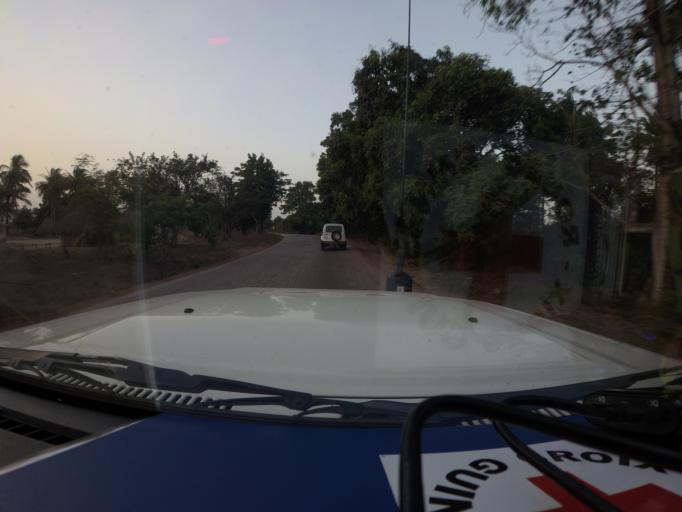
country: GN
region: Kindia
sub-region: Kindia
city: Kindia
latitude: 9.8865
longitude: -13.0550
